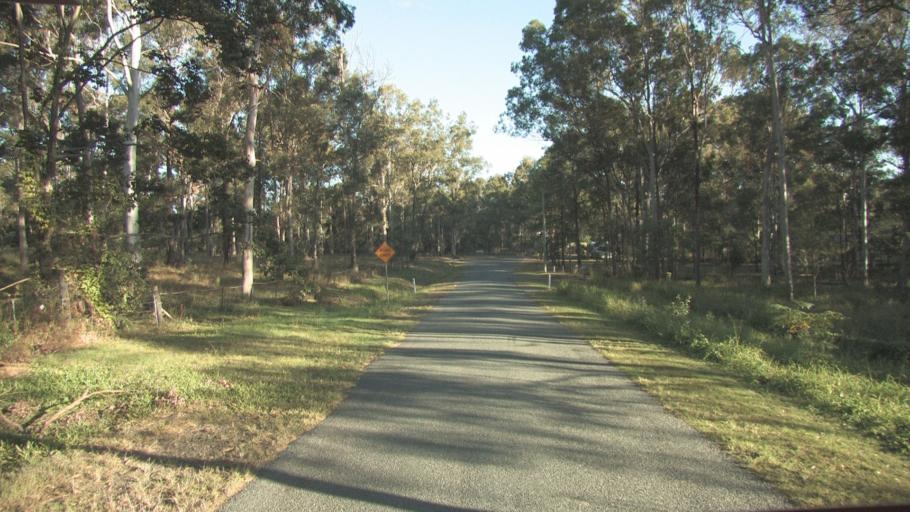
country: AU
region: Queensland
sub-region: Logan
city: Waterford West
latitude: -27.7358
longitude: 153.1511
